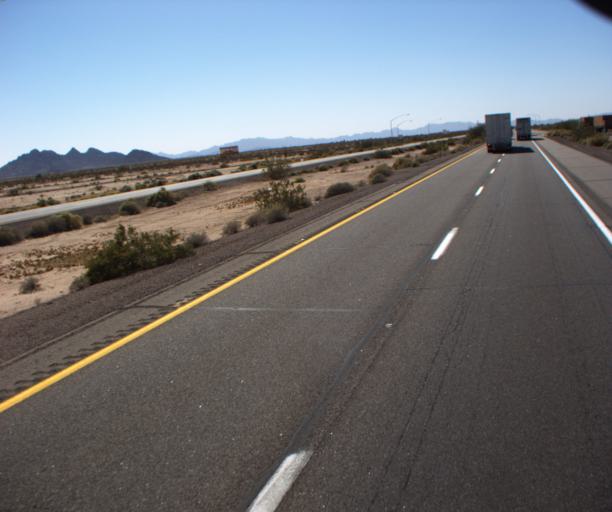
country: US
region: Arizona
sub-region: Yuma County
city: Wellton
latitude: 32.6935
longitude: -113.9544
